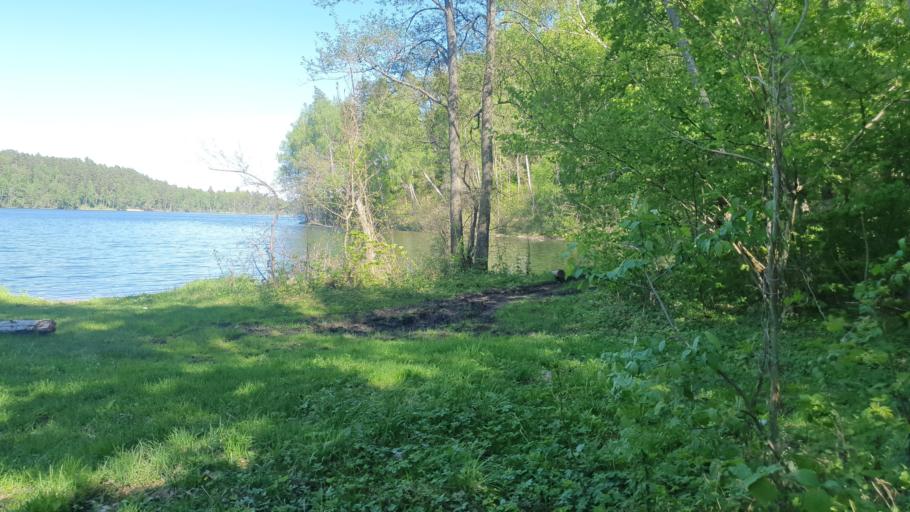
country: LT
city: Nemencine
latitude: 55.0373
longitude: 25.4592
